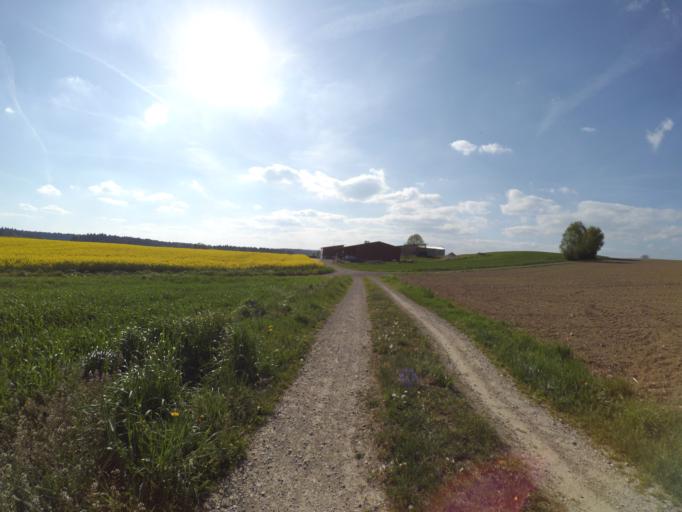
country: CH
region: Thurgau
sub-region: Frauenfeld District
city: Diessenhofen
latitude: 47.6607
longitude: 8.7549
